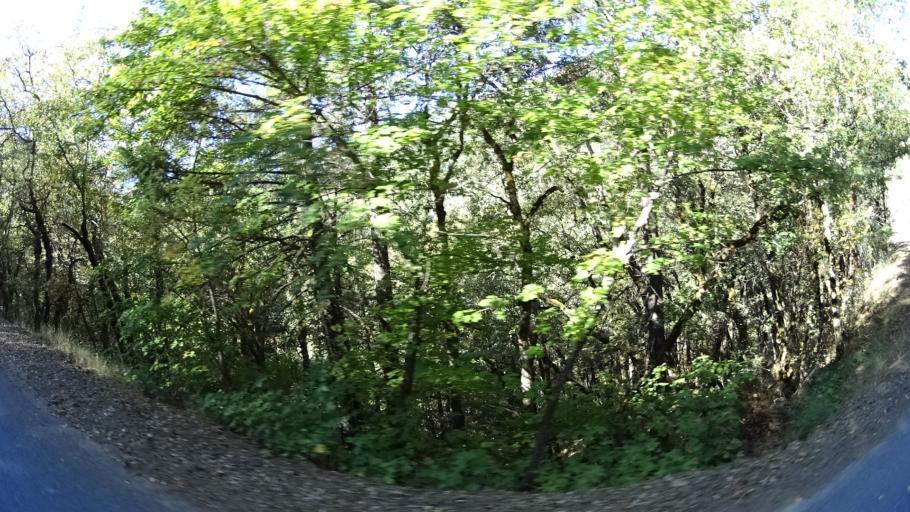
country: US
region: California
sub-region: Humboldt County
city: Willow Creek
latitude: 41.1545
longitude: -123.2092
